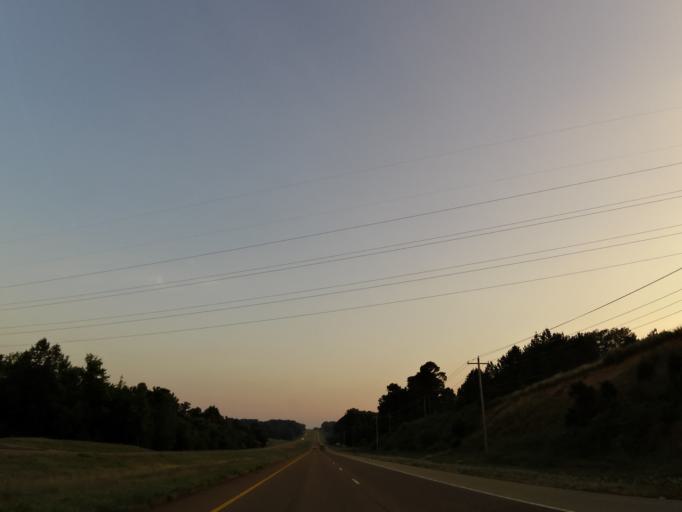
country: US
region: Tennessee
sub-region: Henry County
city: Paris
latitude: 36.2528
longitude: -88.3493
